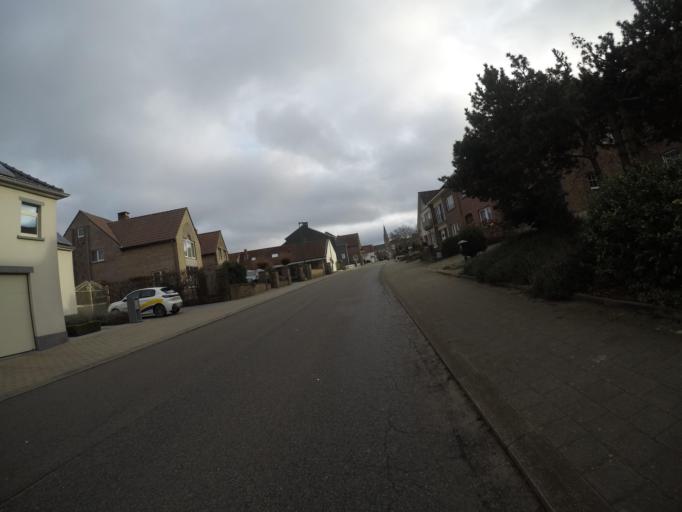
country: BE
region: Flanders
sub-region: Provincie Vlaams-Brabant
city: Ledeberg
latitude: 50.8454
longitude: 4.0698
